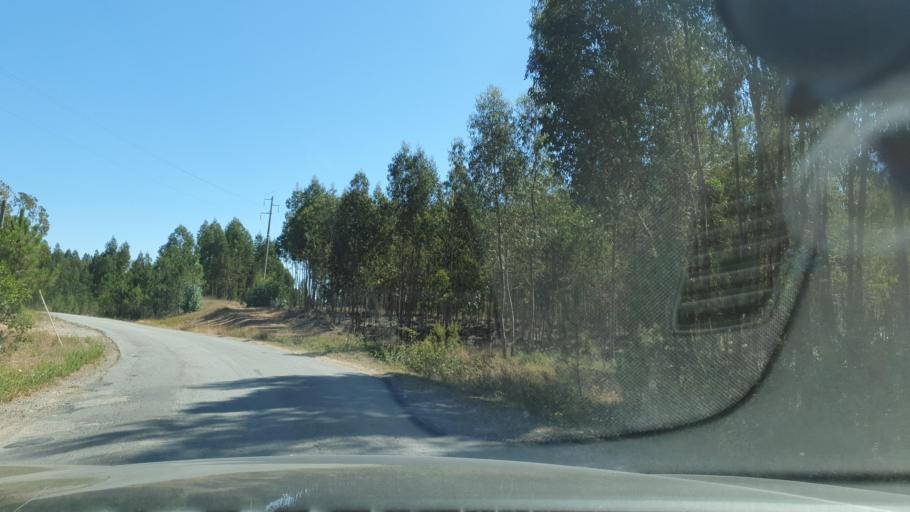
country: PT
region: Beja
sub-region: Odemira
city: Sao Teotonio
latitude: 37.4982
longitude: -8.6647
